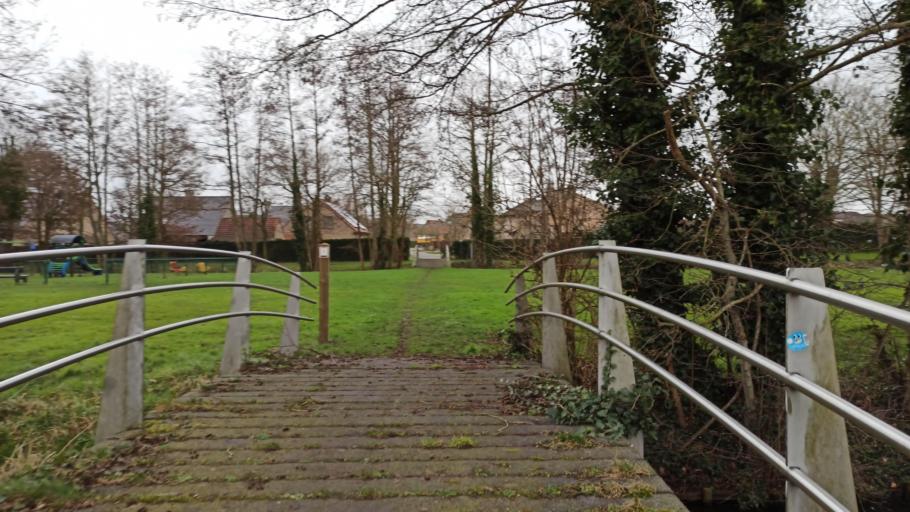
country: BE
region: Flanders
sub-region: Provincie West-Vlaanderen
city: Jabbeke
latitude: 51.1678
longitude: 3.0710
